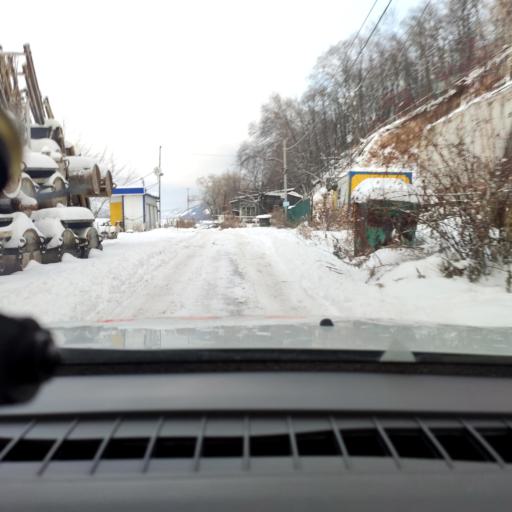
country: RU
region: Samara
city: Samara
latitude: 53.2864
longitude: 50.1907
